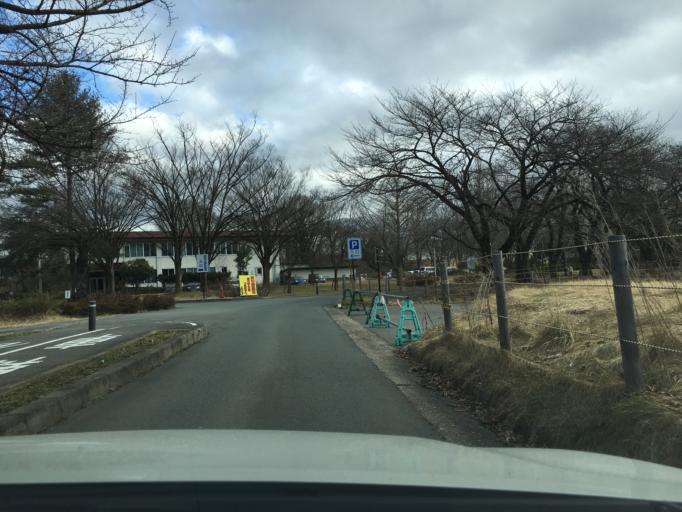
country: JP
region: Yamagata
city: Yamagata-shi
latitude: 38.2571
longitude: 140.3296
